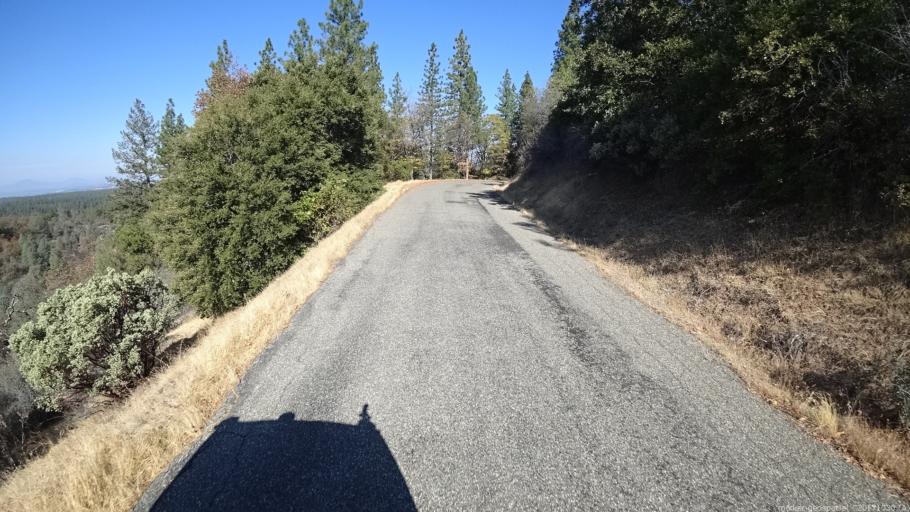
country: US
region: California
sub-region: Shasta County
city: Shingletown
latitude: 40.5844
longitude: -121.8684
